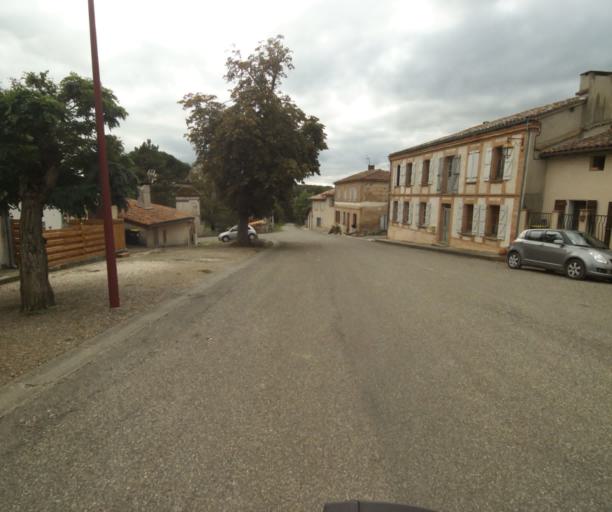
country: FR
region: Midi-Pyrenees
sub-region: Departement du Tarn-et-Garonne
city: Verdun-sur-Garonne
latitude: 43.8425
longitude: 1.1183
